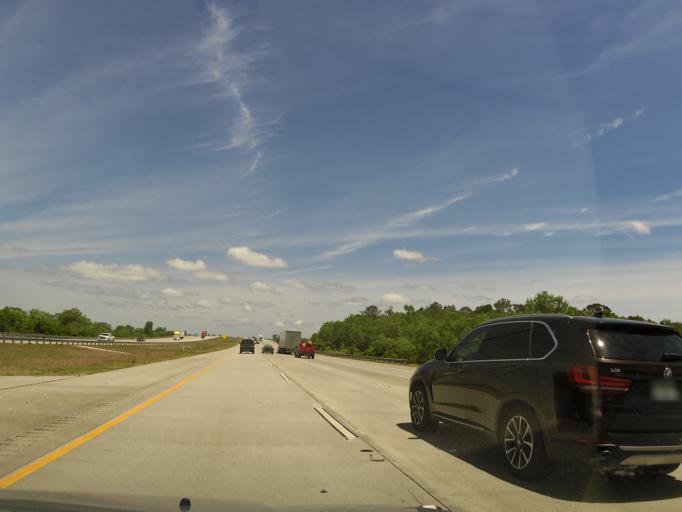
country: US
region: Georgia
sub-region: McIntosh County
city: Darien
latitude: 31.3308
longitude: -81.4696
